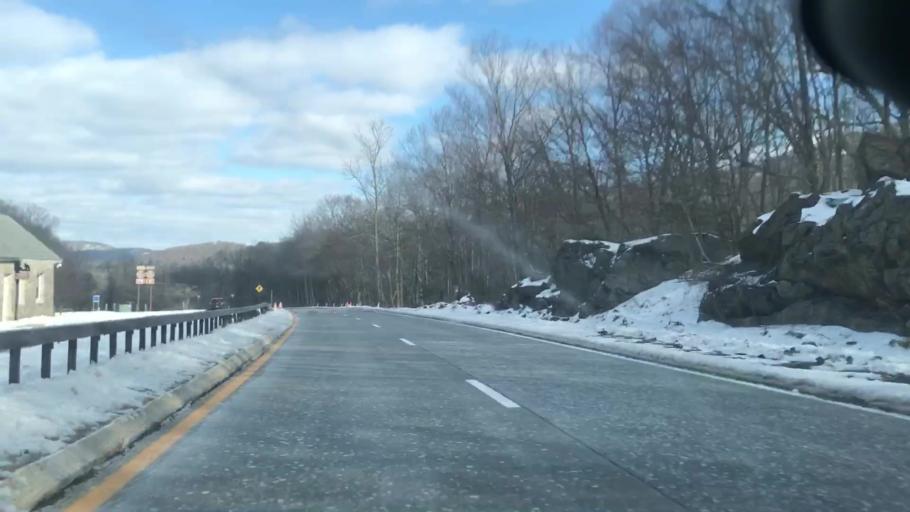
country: US
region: New York
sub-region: Orange County
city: Fort Montgomery
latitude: 41.2886
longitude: -74.0254
